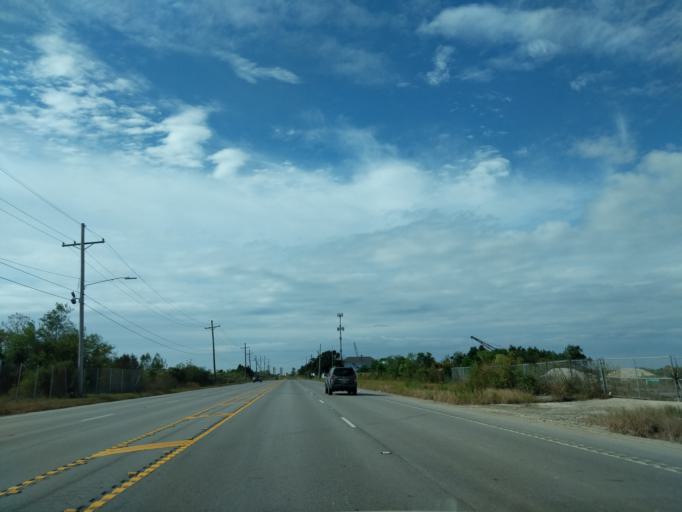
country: US
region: Louisiana
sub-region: Saint Tammany Parish
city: Eden Isle
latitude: 30.0722
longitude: -89.8394
